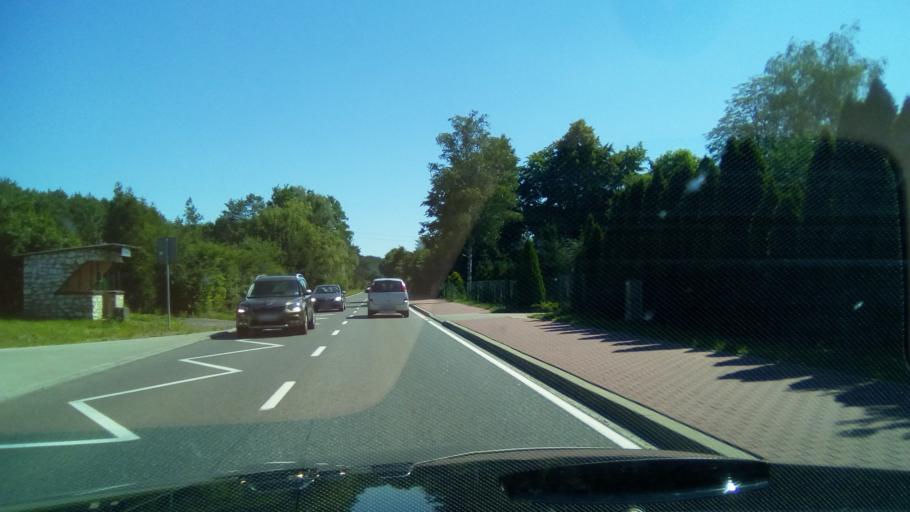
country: PL
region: Lodz Voivodeship
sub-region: Powiat tomaszowski
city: Inowlodz
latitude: 51.5237
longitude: 20.2092
